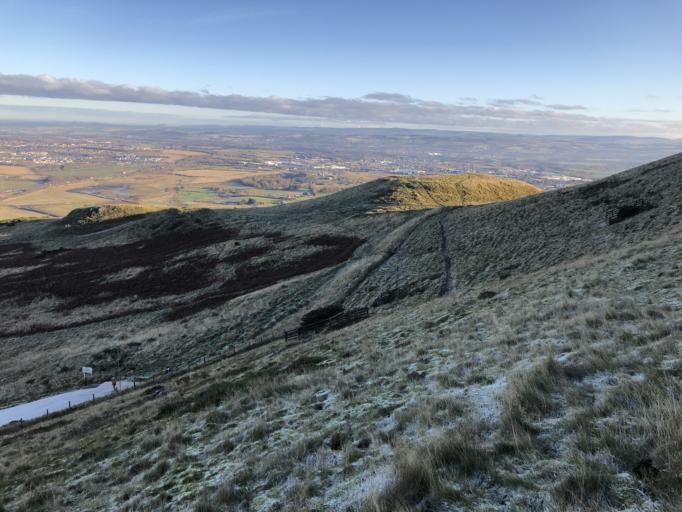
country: GB
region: Scotland
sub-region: Edinburgh
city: Colinton
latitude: 55.8837
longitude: -3.2119
